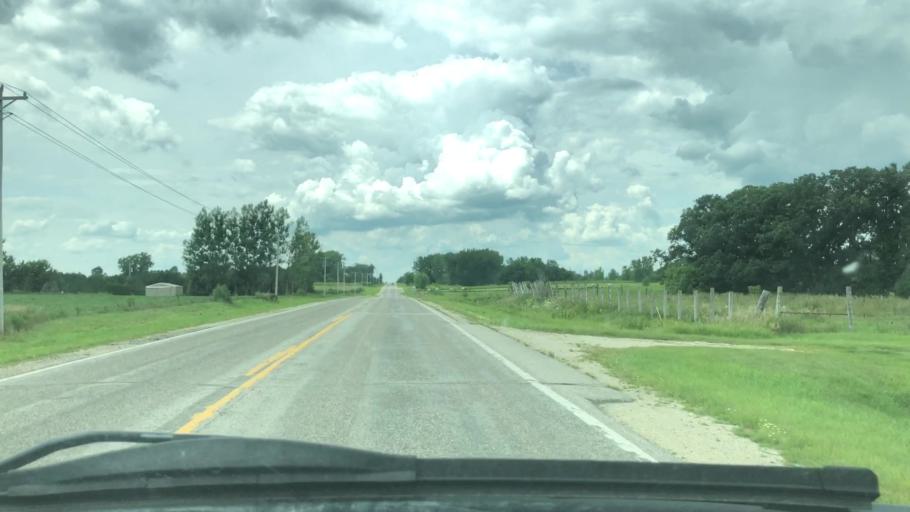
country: US
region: Minnesota
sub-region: Olmsted County
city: Stewartville
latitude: 43.8627
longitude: -92.5106
